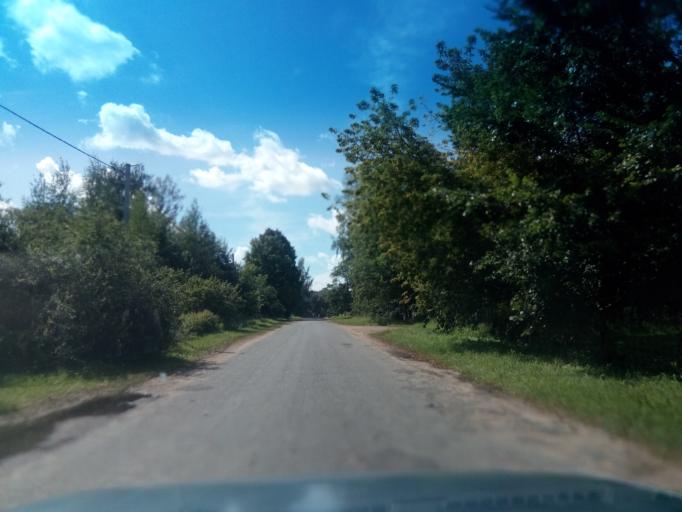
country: BY
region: Vitebsk
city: Dzisna
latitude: 55.6784
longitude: 28.3522
